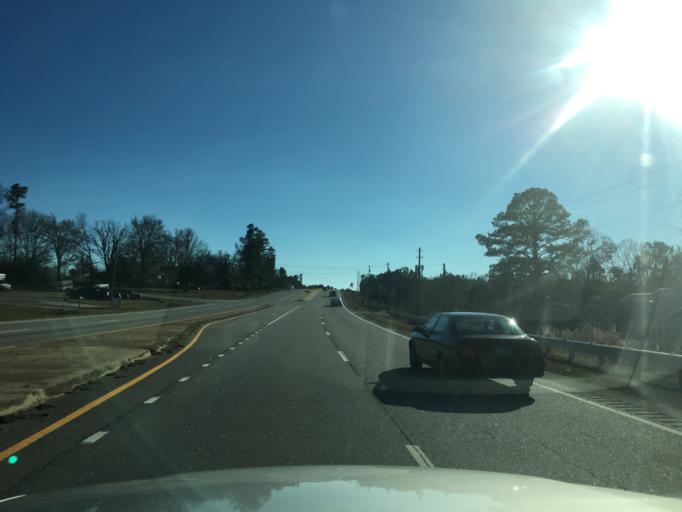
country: US
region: Georgia
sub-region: Carroll County
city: Carrollton
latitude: 33.5247
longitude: -85.0748
